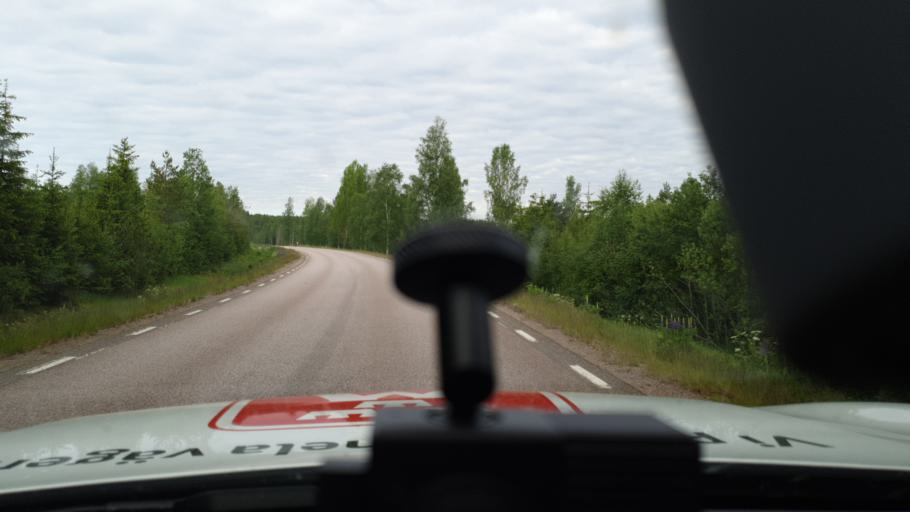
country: SE
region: Vaermland
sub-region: Torsby Kommun
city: Torsby
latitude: 60.1197
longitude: 12.9432
